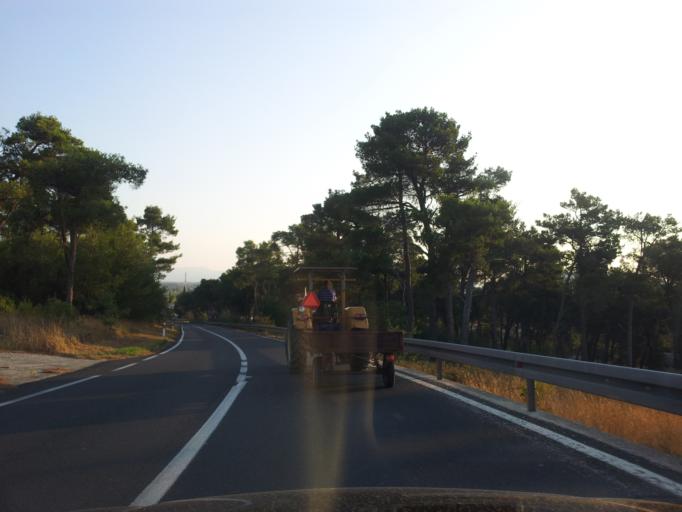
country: HR
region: Zadarska
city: Biograd na Moru
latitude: 43.9577
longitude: 15.4738
